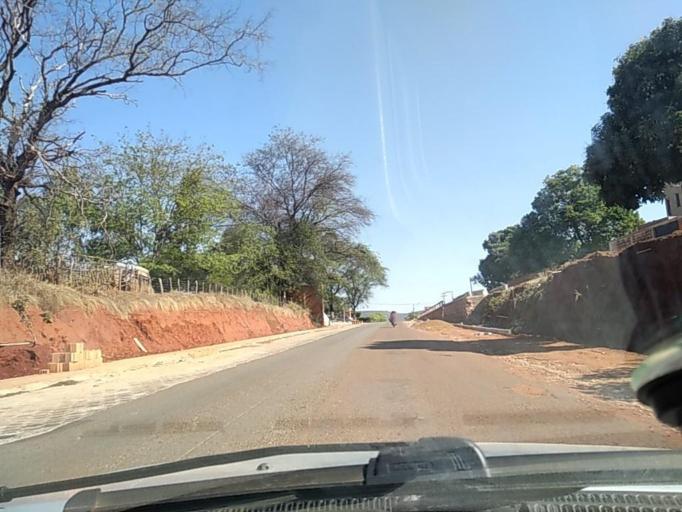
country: BR
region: Bahia
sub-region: Caetite
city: Caetite
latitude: -14.0521
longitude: -42.4846
